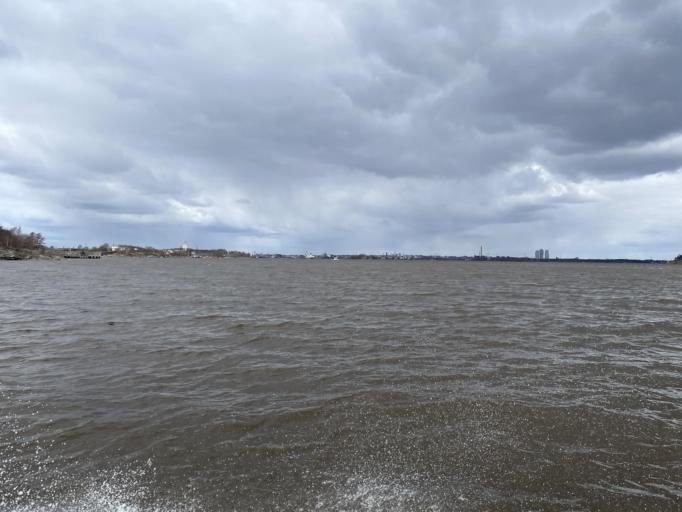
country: FI
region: Uusimaa
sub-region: Helsinki
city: Helsinki
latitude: 60.1392
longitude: 25.0136
